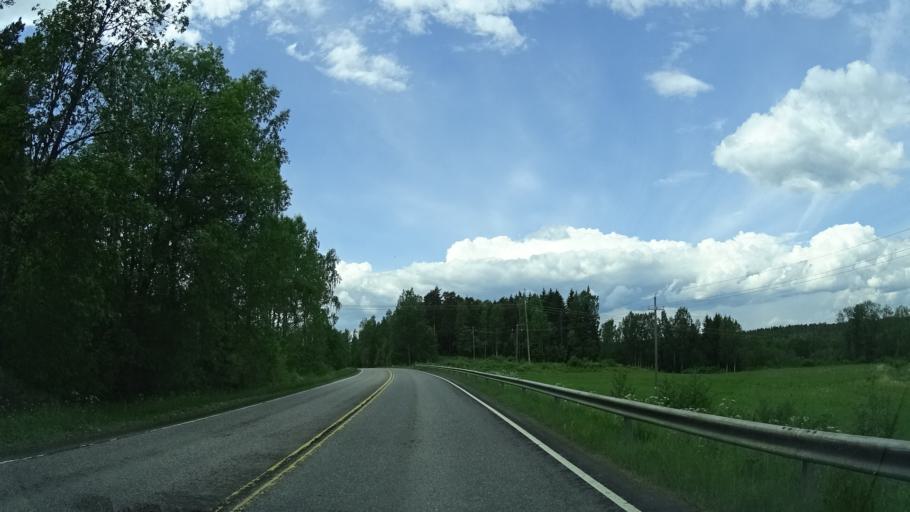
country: FI
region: Uusimaa
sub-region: Helsinki
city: Espoo
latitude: 60.2000
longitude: 24.5532
